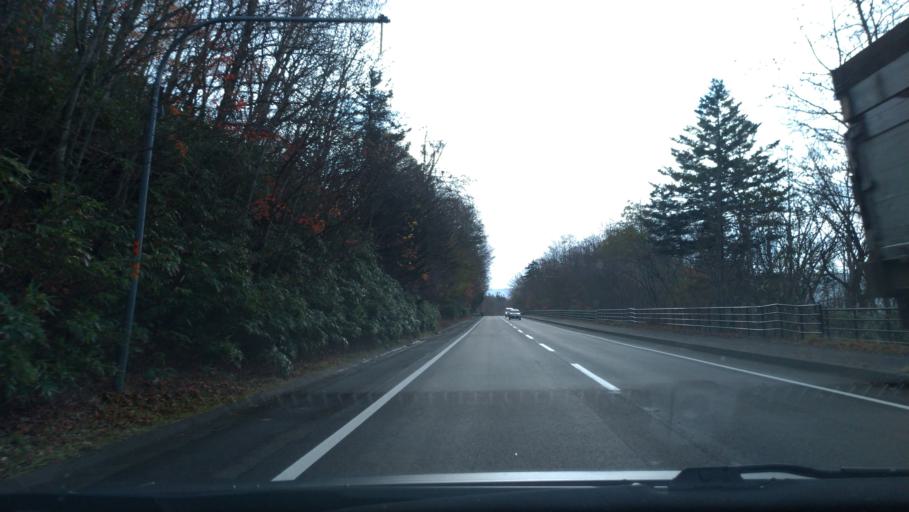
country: JP
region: Hokkaido
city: Shiraoi
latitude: 42.7213
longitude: 141.3295
